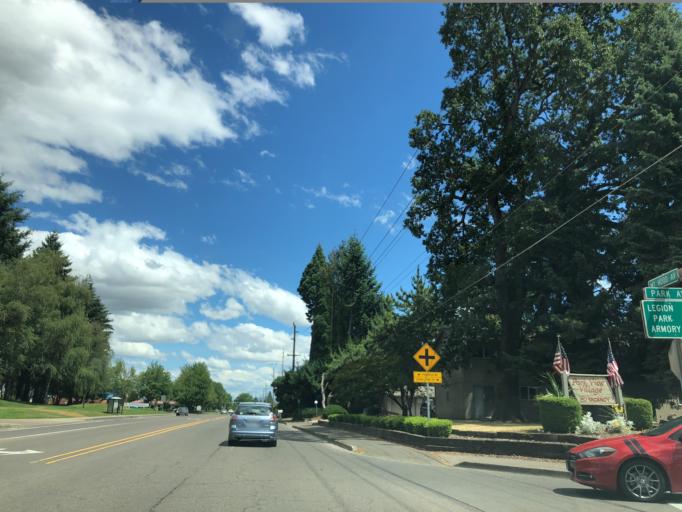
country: US
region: Oregon
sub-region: Marion County
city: Woodburn
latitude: 45.1514
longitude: -122.8413
